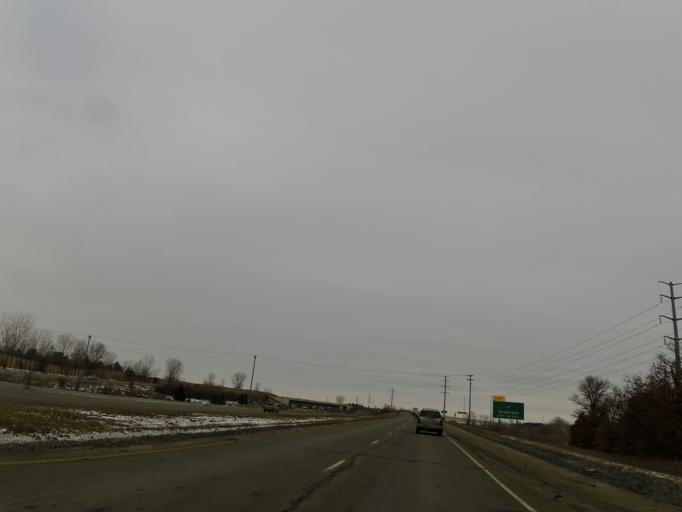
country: US
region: Minnesota
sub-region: Scott County
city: Savage
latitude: 44.7835
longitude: -93.3953
